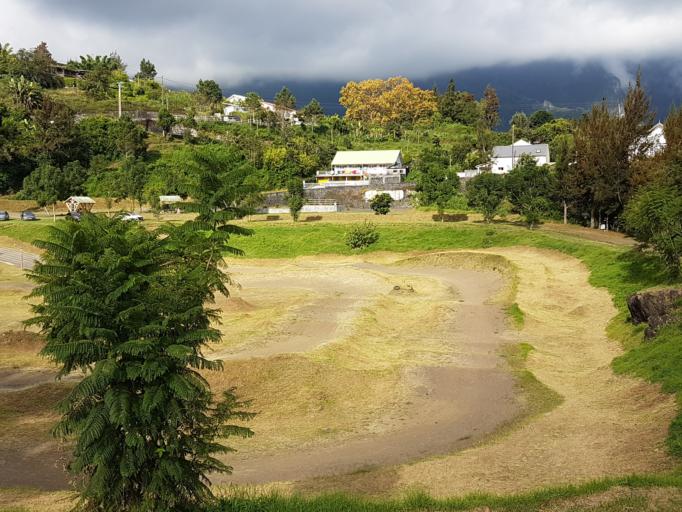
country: RE
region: Reunion
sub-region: Reunion
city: Cilaos
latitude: -21.1322
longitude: 55.4724
